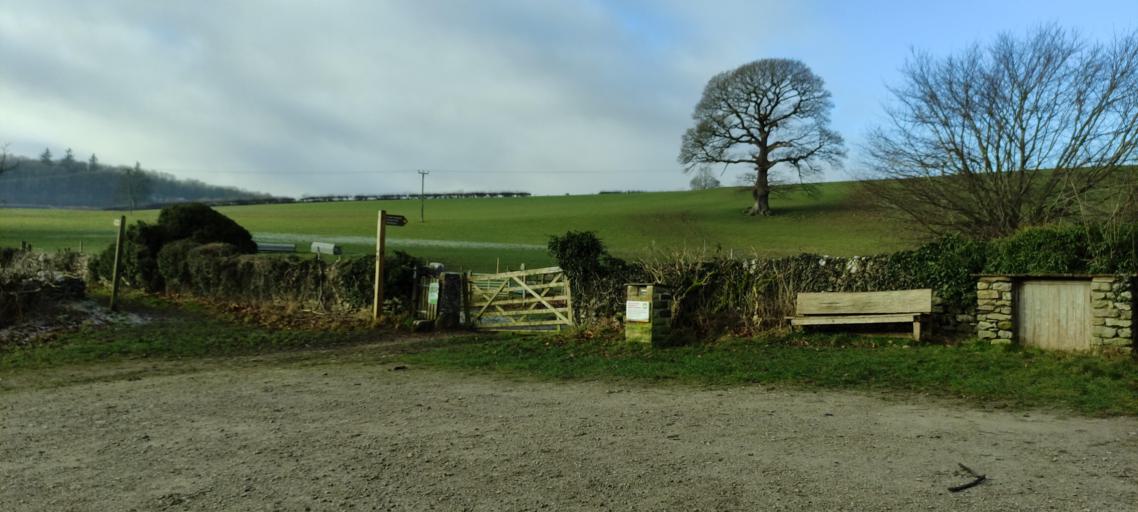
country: GB
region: England
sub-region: Cumbria
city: Milnthorpe
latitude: 54.2127
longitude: -2.7749
